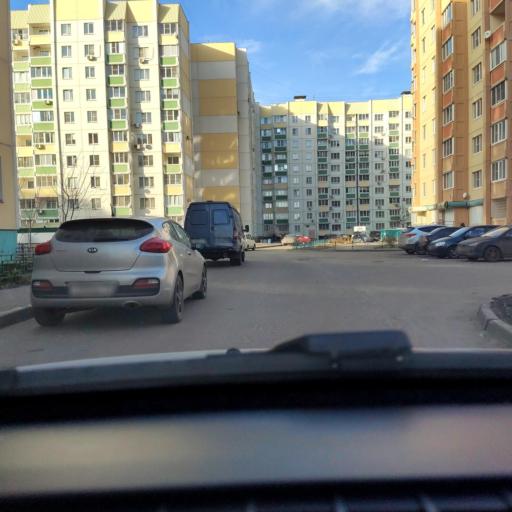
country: RU
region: Voronezj
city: Pridonskoy
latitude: 51.6209
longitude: 39.0626
